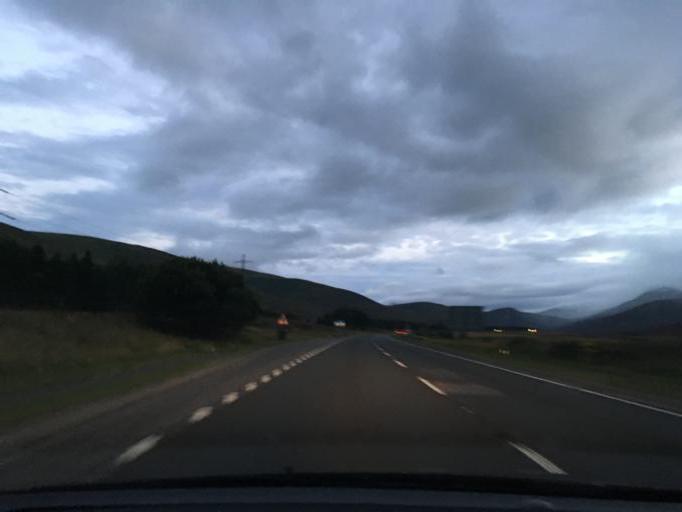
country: GB
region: Scotland
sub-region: Highland
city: Kingussie
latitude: 56.9135
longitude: -4.2356
